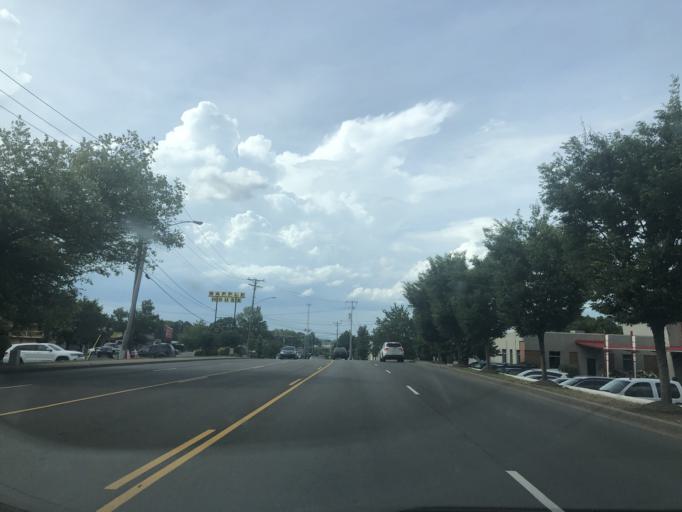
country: US
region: Tennessee
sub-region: Davidson County
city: Oak Hill
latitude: 36.0835
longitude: -86.7615
